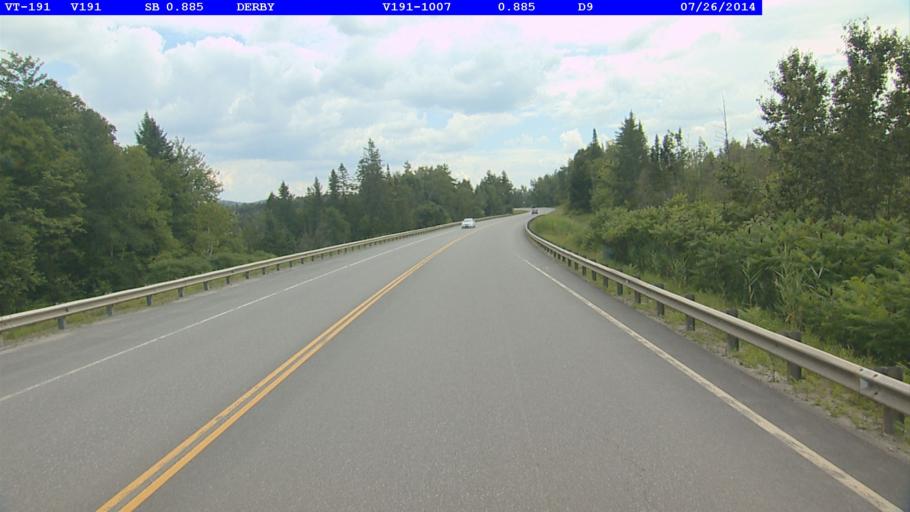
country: US
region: Vermont
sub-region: Orleans County
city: Newport
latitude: 44.9306
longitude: -72.1813
